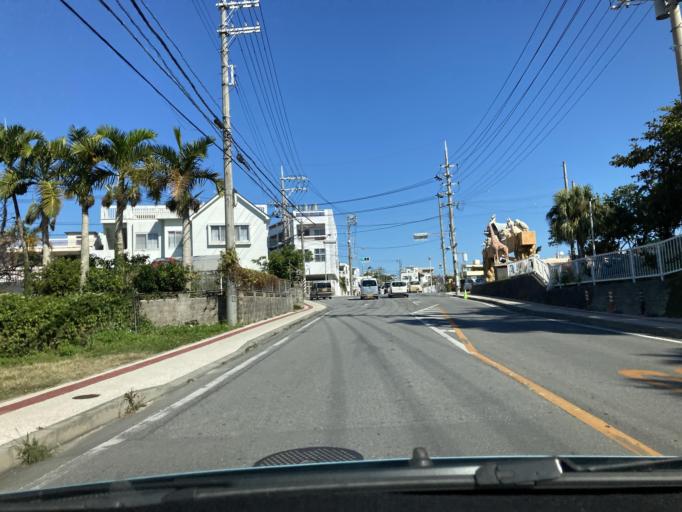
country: JP
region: Okinawa
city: Okinawa
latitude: 26.3274
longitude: 127.8022
